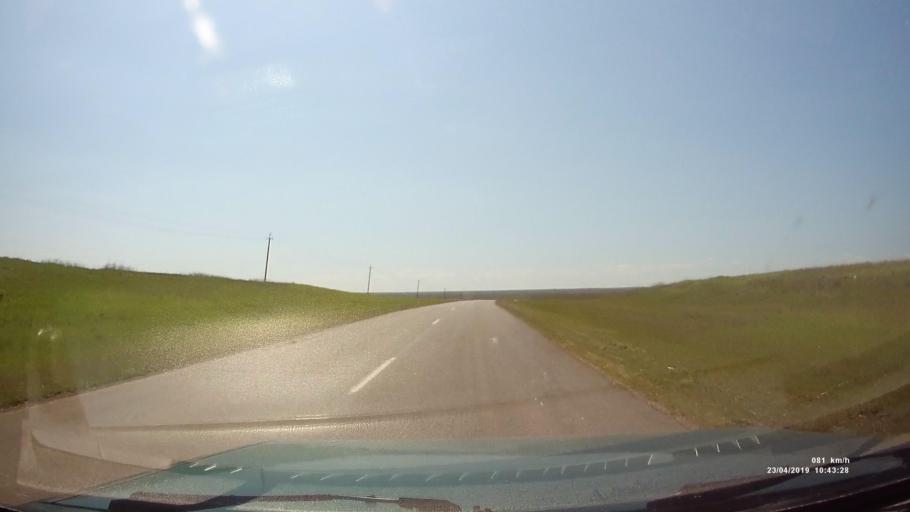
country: RU
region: Kalmykiya
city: Yashalta
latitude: 46.4699
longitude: 42.6499
